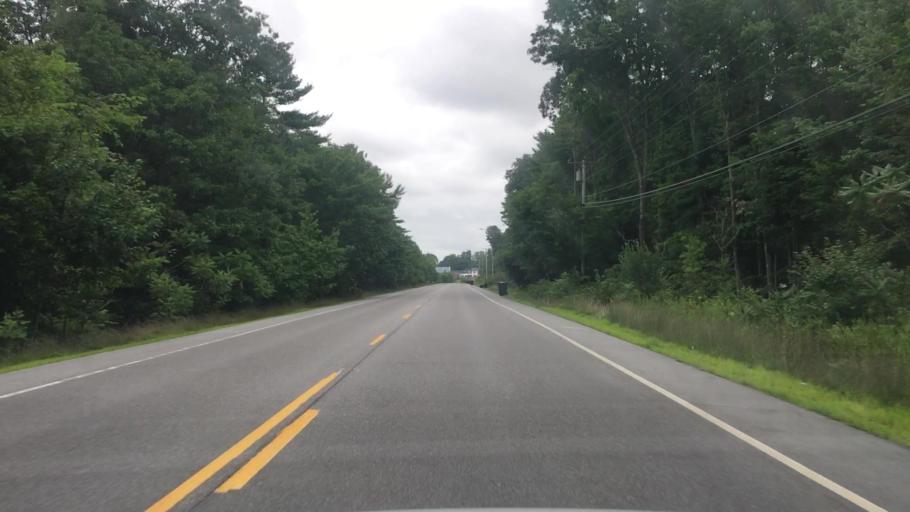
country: US
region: Maine
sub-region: York County
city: Biddeford
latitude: 43.5254
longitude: -70.4954
